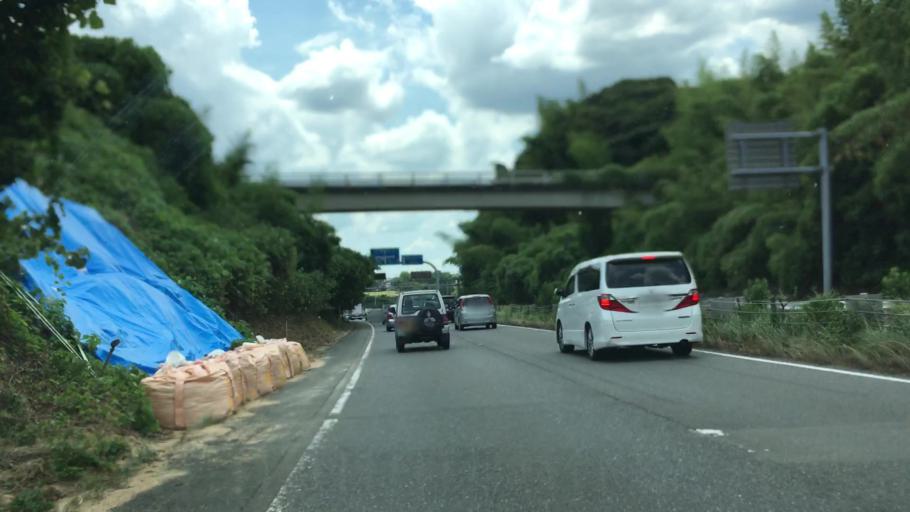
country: JP
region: Fukuoka
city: Chikushino-shi
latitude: 33.4380
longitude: 130.5256
